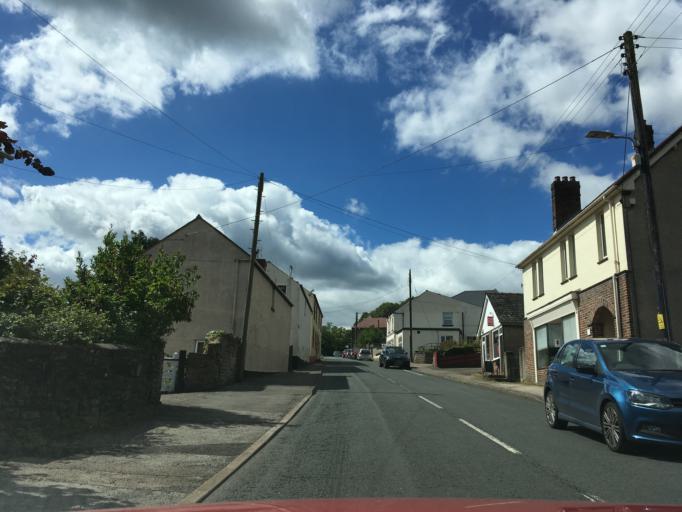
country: GB
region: England
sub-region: Gloucestershire
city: Bream
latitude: 51.7537
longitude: -2.5727
